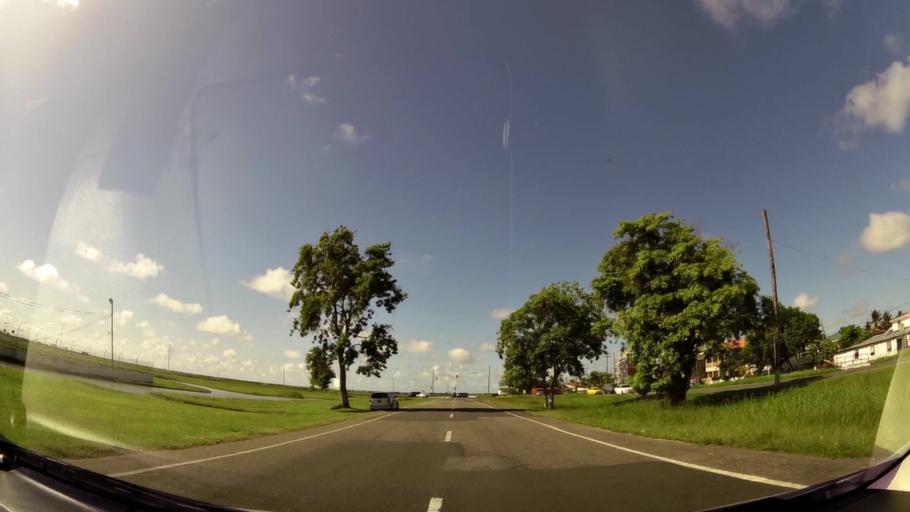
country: GY
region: Demerara-Mahaica
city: Georgetown
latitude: 6.8238
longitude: -58.1438
